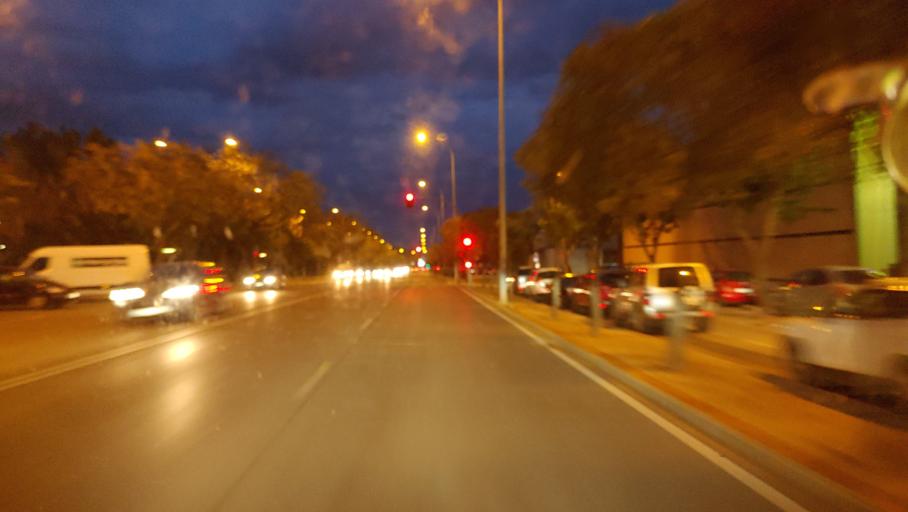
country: ES
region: Castille-La Mancha
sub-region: Provincia de Ciudad Real
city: Ciudad Real
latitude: 38.9810
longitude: -3.9162
